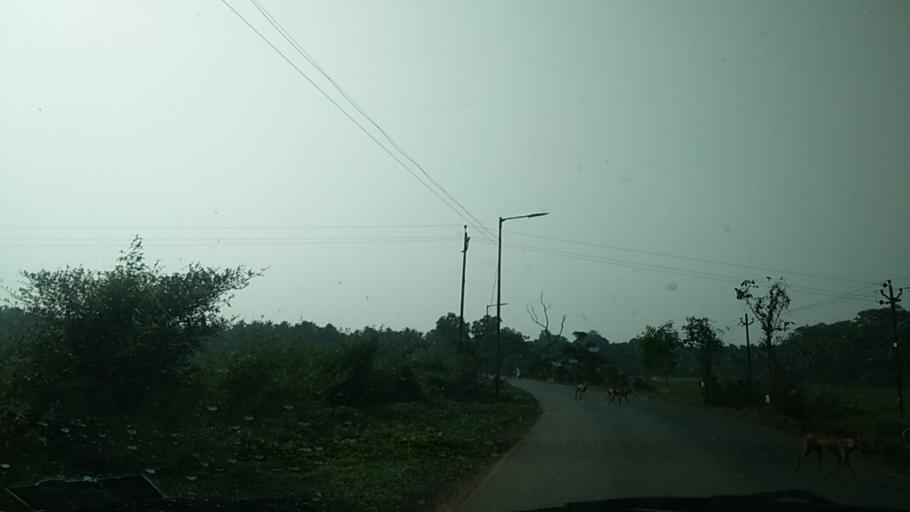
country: IN
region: Goa
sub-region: South Goa
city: Raia
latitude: 15.3072
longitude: 73.9423
